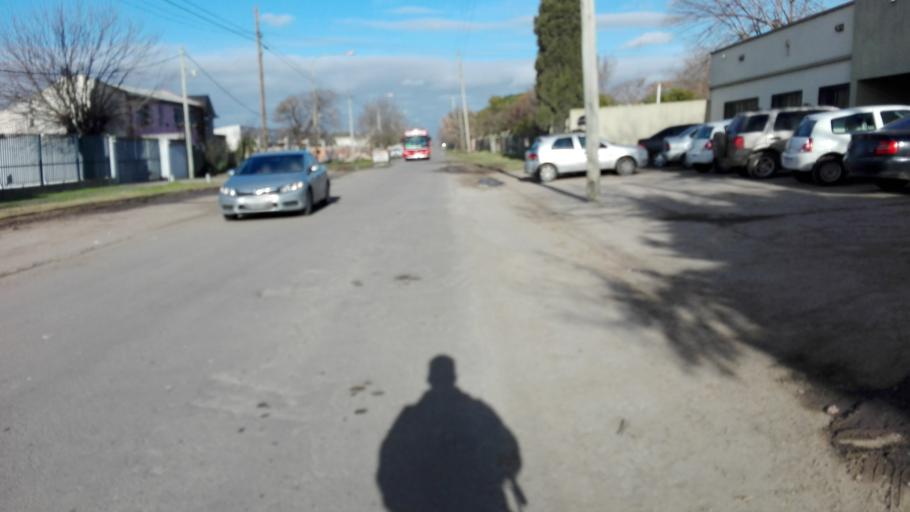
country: AR
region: Buenos Aires
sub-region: Partido de La Plata
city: La Plata
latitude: -34.9148
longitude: -58.0240
